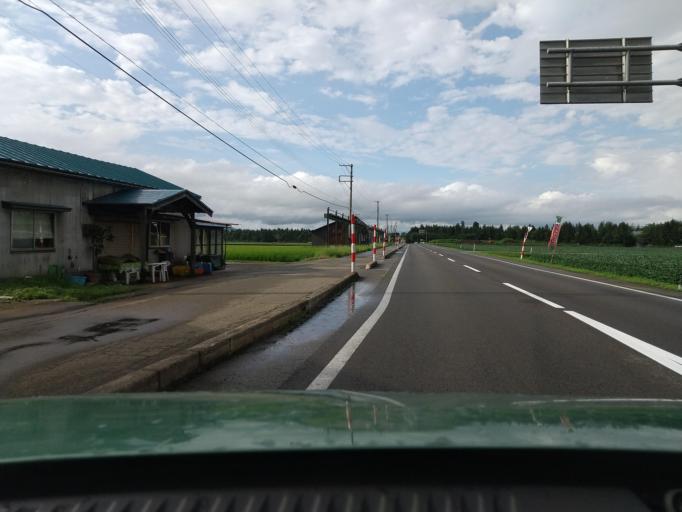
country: JP
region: Akita
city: Omagari
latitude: 39.3952
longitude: 140.4734
